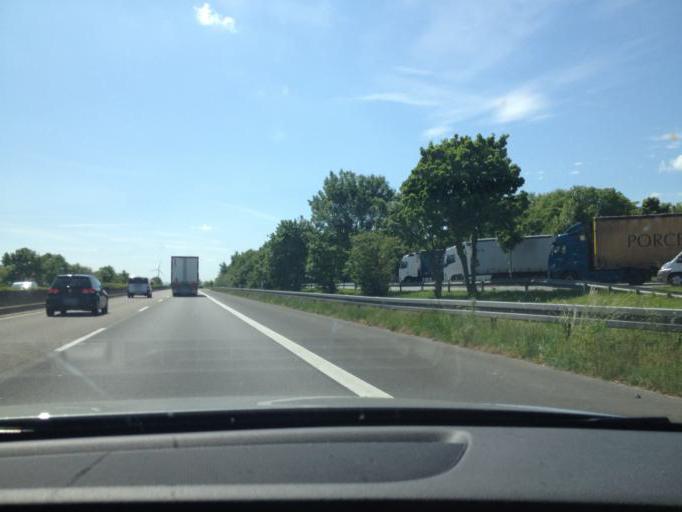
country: DE
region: North Rhine-Westphalia
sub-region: Regierungsbezirk Koln
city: Weilerswist
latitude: 50.7419
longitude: 6.8003
